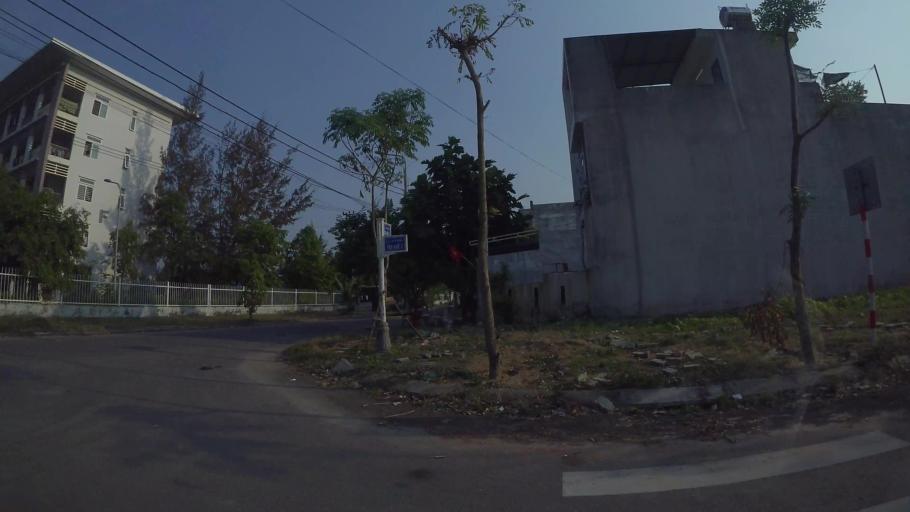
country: VN
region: Da Nang
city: Ngu Hanh Son
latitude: 15.9768
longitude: 108.2565
